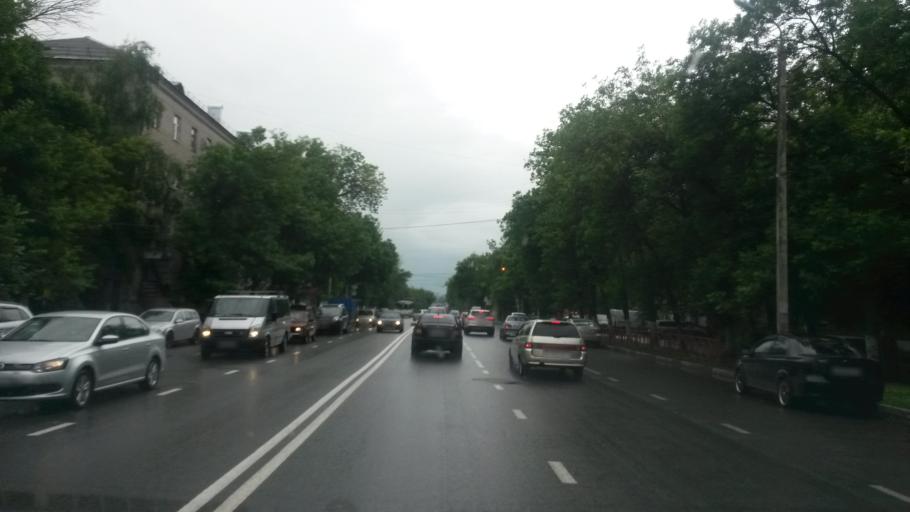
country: RU
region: Jaroslavl
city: Yaroslavl
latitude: 57.6260
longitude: 39.8578
